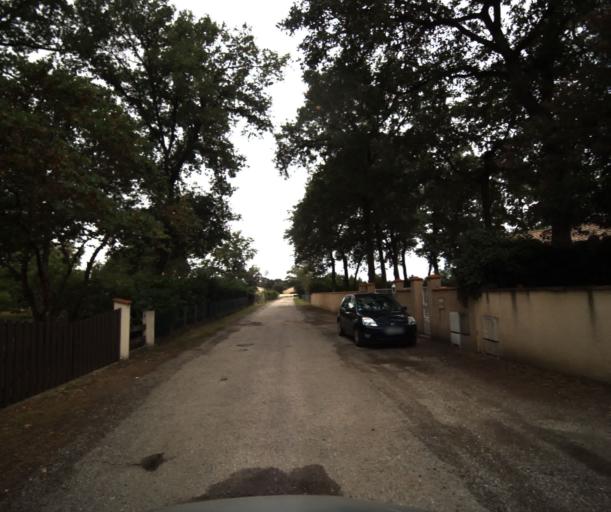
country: FR
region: Midi-Pyrenees
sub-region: Departement de la Haute-Garonne
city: Roquettes
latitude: 43.4926
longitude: 1.3826
